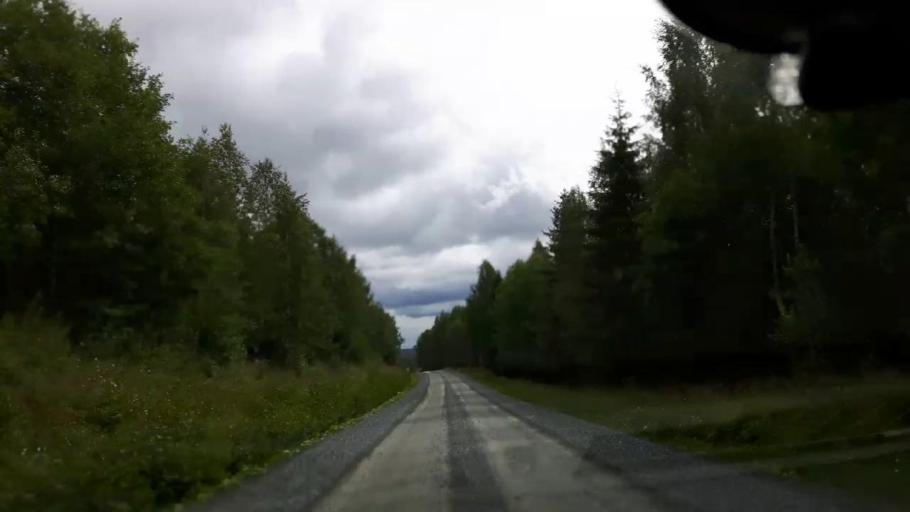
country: SE
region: Jaemtland
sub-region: Krokoms Kommun
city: Valla
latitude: 63.5880
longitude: 14.1495
